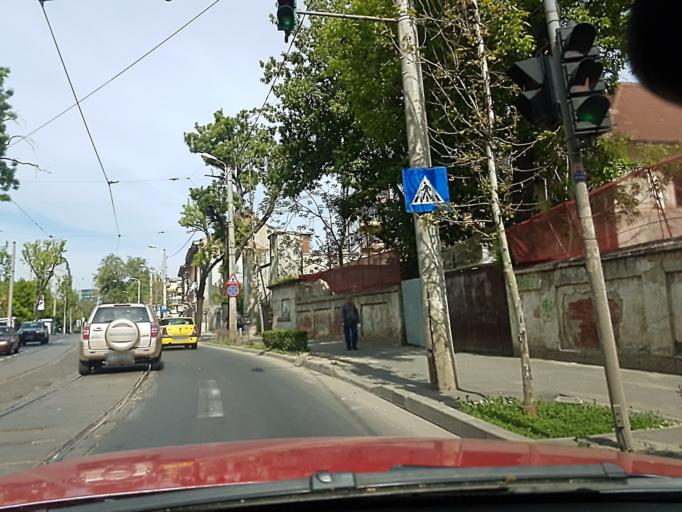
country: RO
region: Bucuresti
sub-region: Municipiul Bucuresti
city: Bucharest
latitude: 44.4232
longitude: 26.1286
